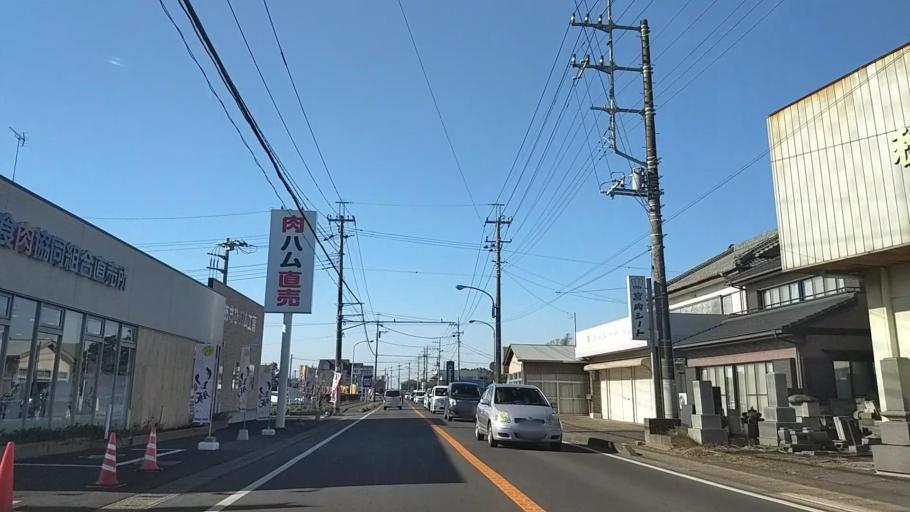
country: JP
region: Chiba
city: Asahi
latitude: 35.7238
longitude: 140.6242
